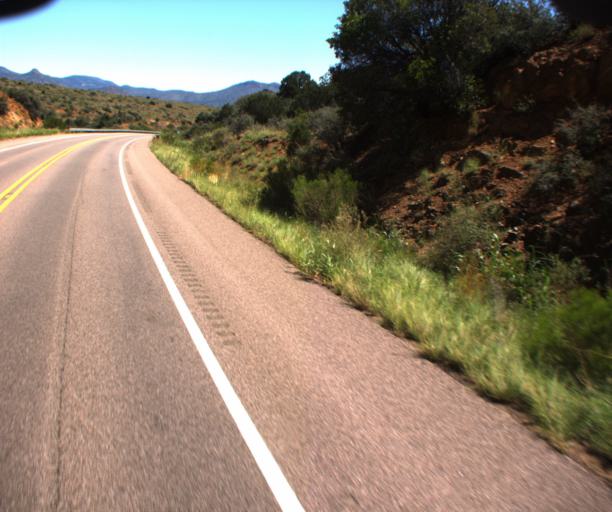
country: US
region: Arizona
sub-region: Gila County
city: Globe
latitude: 33.5486
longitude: -110.6911
